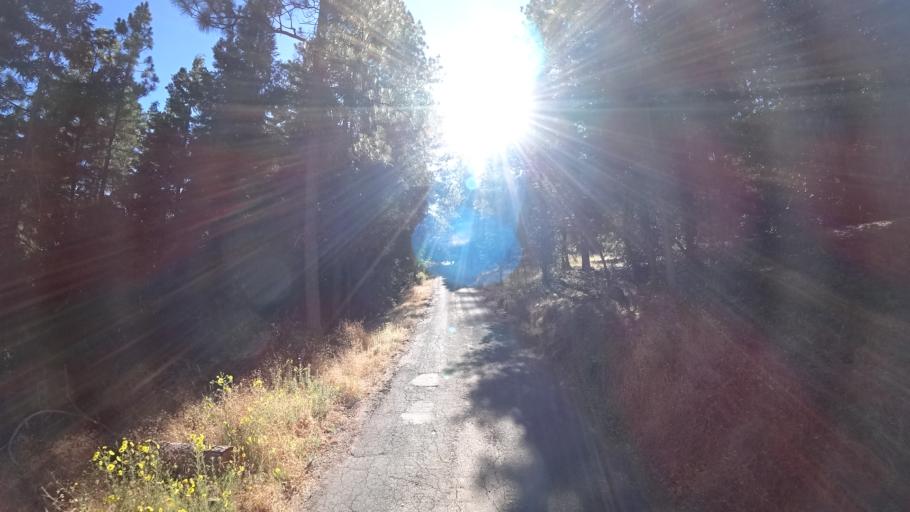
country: US
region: California
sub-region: Amador County
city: Pioneer
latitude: 38.3850
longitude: -120.5604
